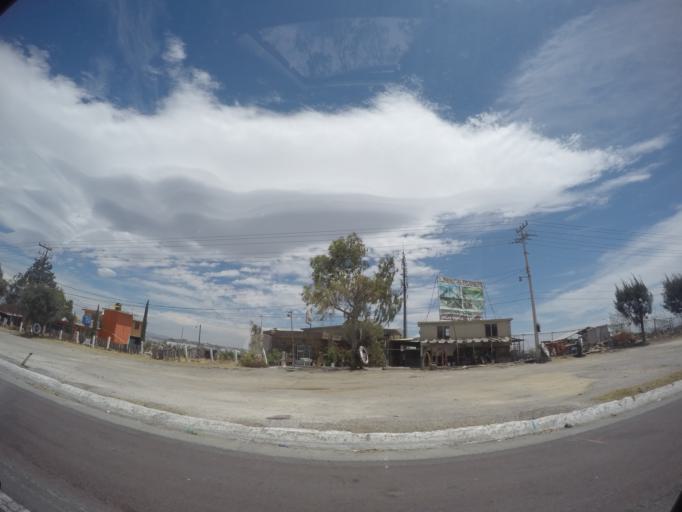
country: MX
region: Mexico
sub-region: Cuautitlan
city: Barrio Tlatenco
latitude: 19.7356
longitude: -99.2107
